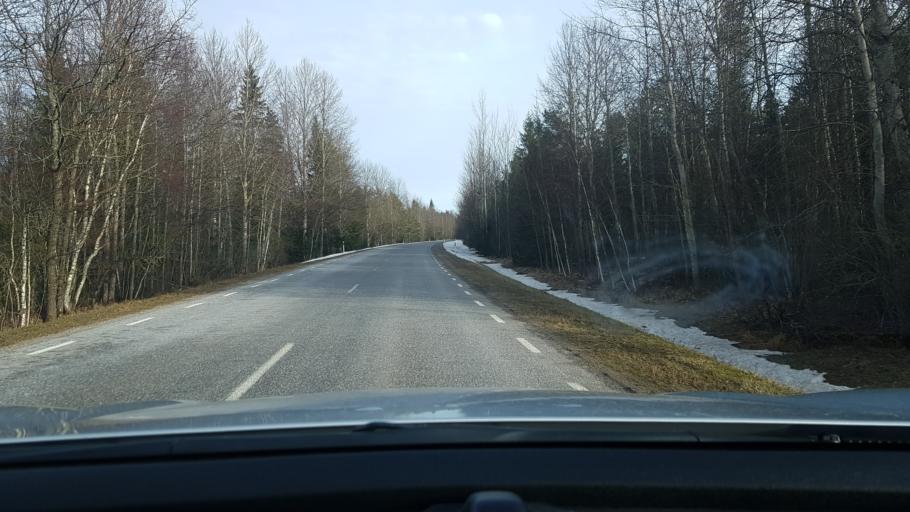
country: EE
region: Saare
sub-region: Kuressaare linn
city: Kuressaare
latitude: 58.4191
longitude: 22.6638
